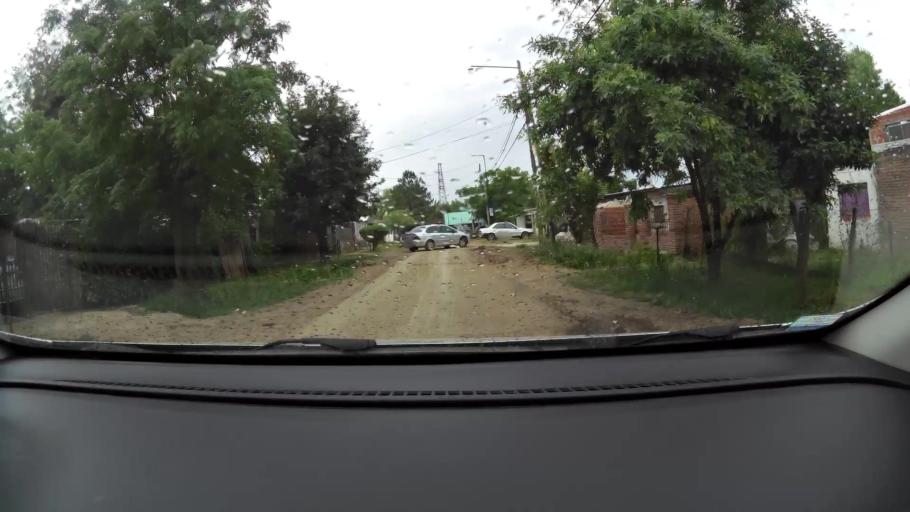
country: AR
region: Buenos Aires
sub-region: Partido de Zarate
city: Zarate
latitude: -34.1151
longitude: -59.0391
